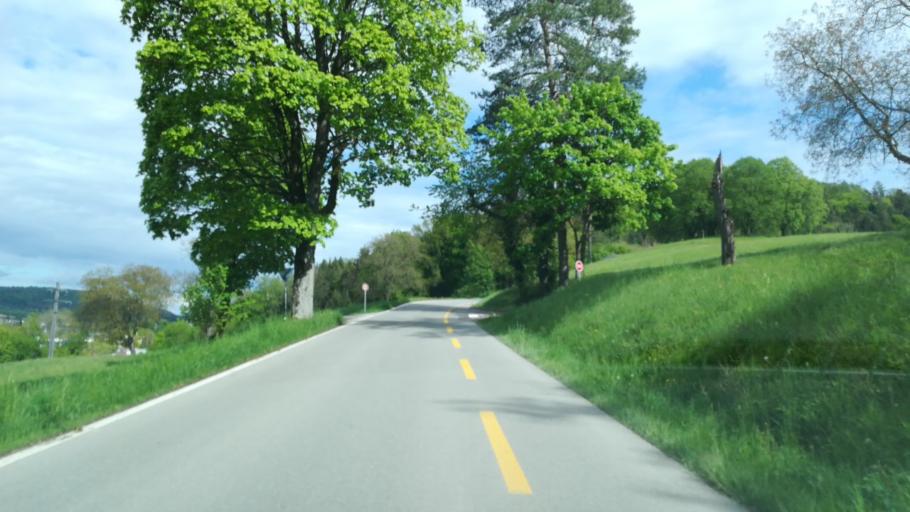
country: CH
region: Schaffhausen
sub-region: Bezirk Reiat
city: Thayngen
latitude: 47.7399
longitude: 8.7117
